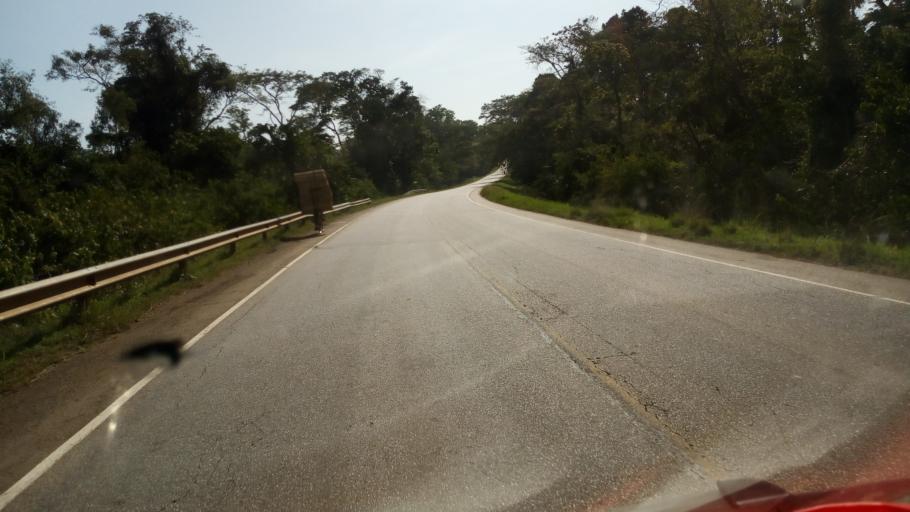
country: UG
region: Eastern Region
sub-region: Busia District
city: Busia
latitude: 0.5392
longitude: 34.0080
